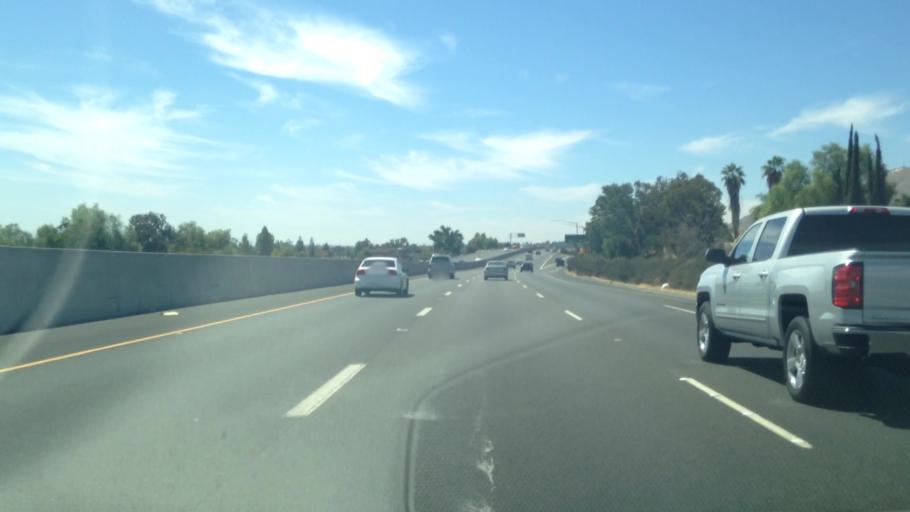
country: US
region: California
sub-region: Riverside County
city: Moreno Valley
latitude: 33.9389
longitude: -117.2203
